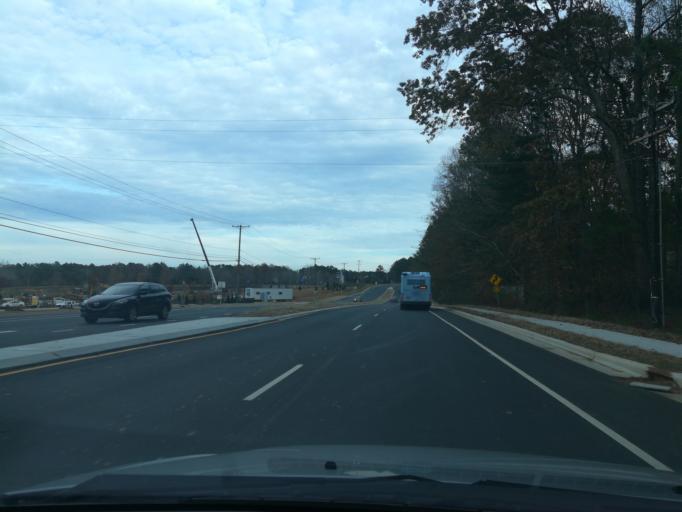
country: US
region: North Carolina
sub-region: Orange County
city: Chapel Hill
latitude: 35.9694
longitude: -79.0657
